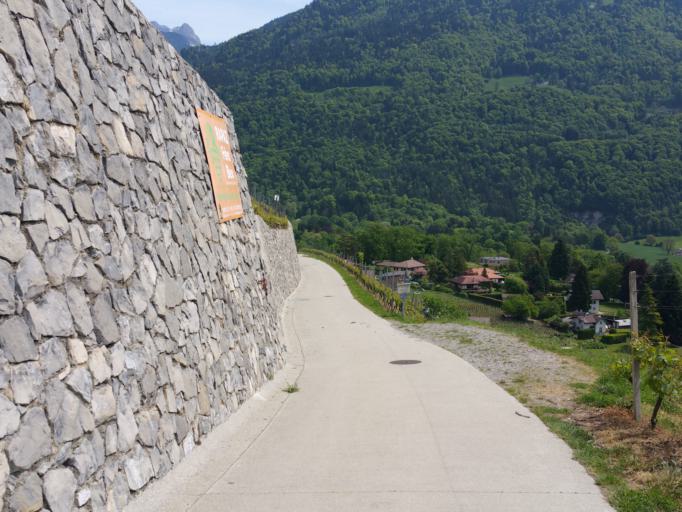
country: CH
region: Vaud
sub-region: Aigle District
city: Bex
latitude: 46.2552
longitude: 7.0145
